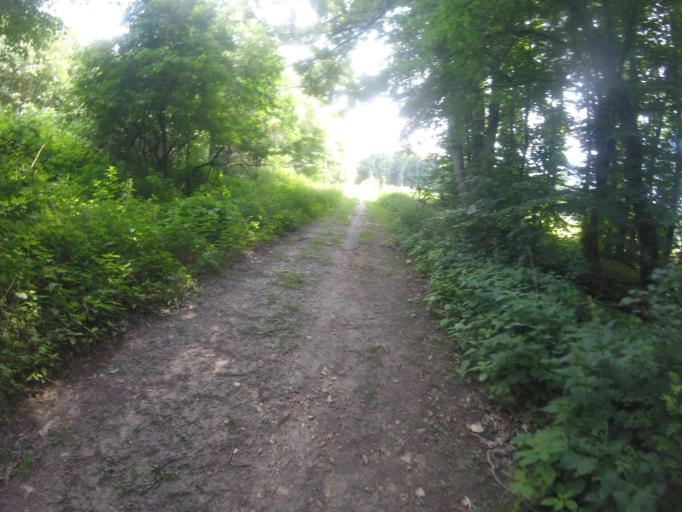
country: HU
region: Fejer
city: Szarliget
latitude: 47.5053
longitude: 18.4306
